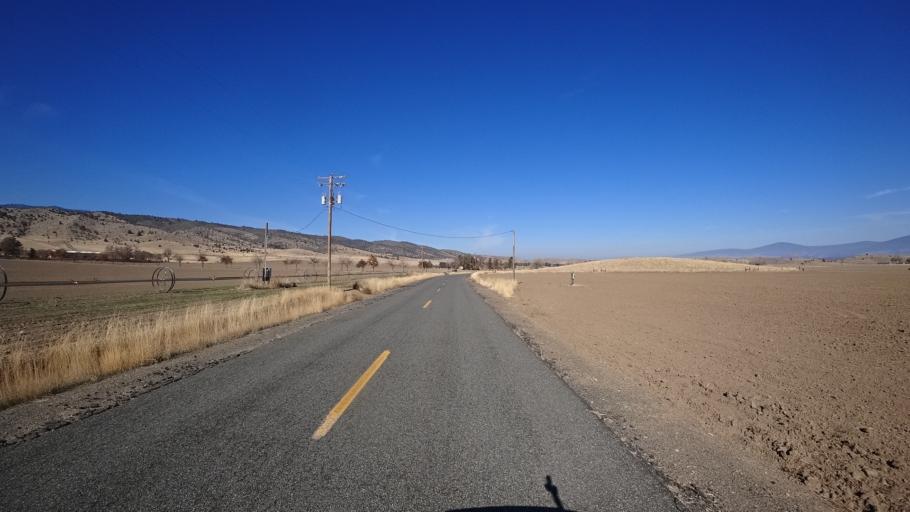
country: US
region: California
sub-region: Siskiyou County
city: Montague
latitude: 41.5709
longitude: -122.5490
